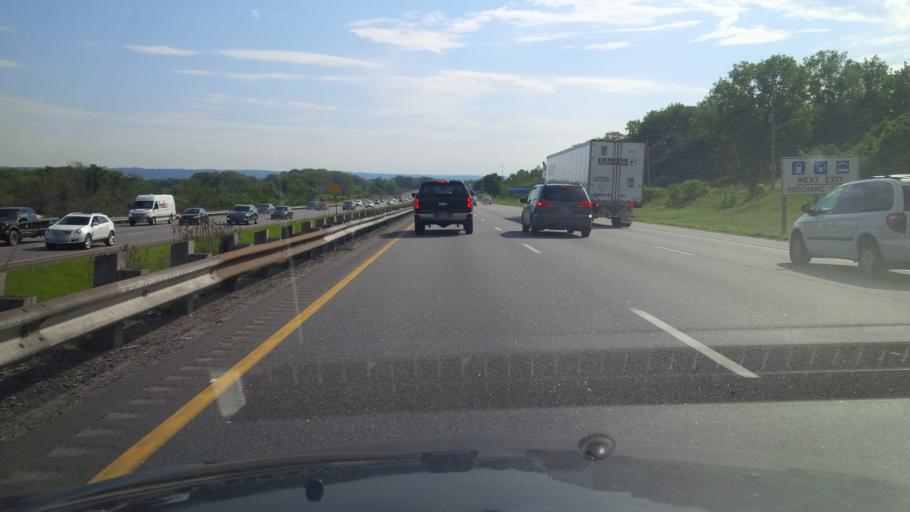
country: CA
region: Ontario
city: Hamilton
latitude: 43.3026
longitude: -79.8735
